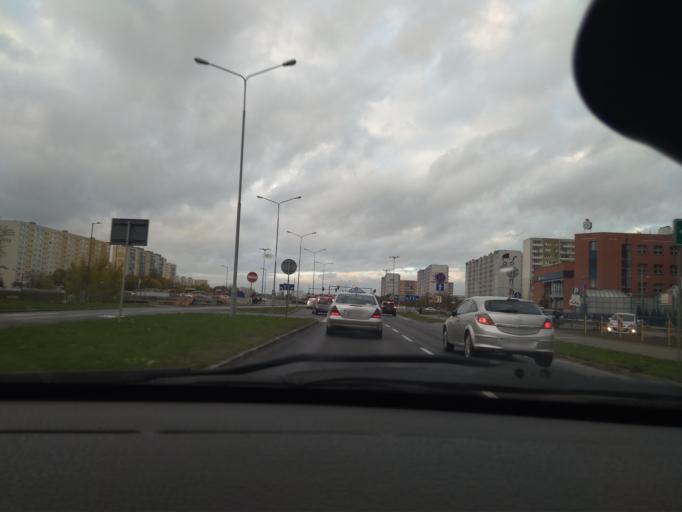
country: PL
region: Greater Poland Voivodeship
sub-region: Poznan
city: Poznan
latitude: 52.4490
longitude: 16.9205
